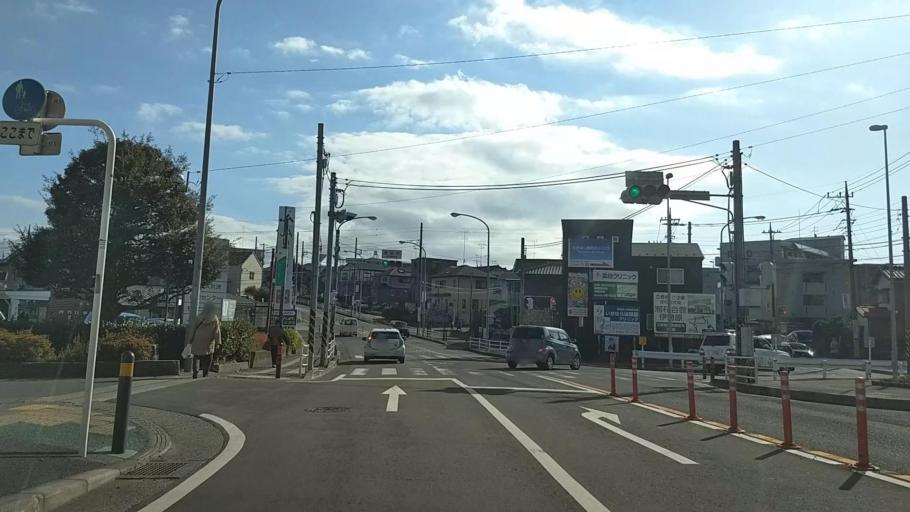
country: JP
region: Kanagawa
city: Isehara
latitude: 35.4010
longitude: 139.3141
